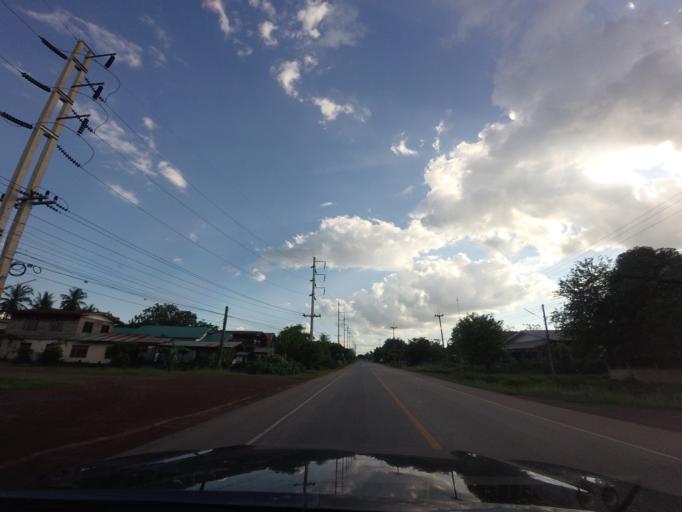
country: TH
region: Changwat Udon Thani
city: Thung Fon
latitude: 17.4572
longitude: 103.1879
